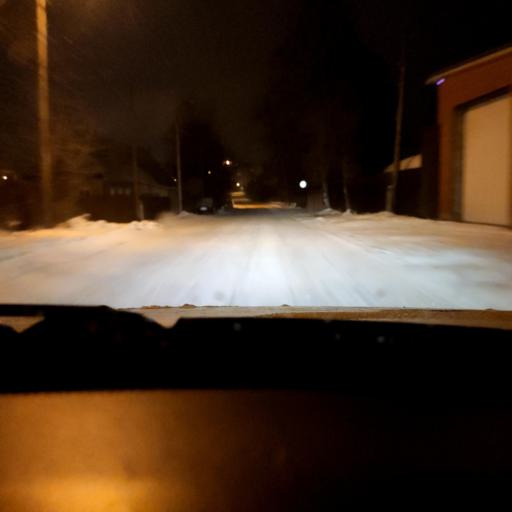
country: RU
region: Perm
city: Polazna
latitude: 58.1247
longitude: 56.3970
